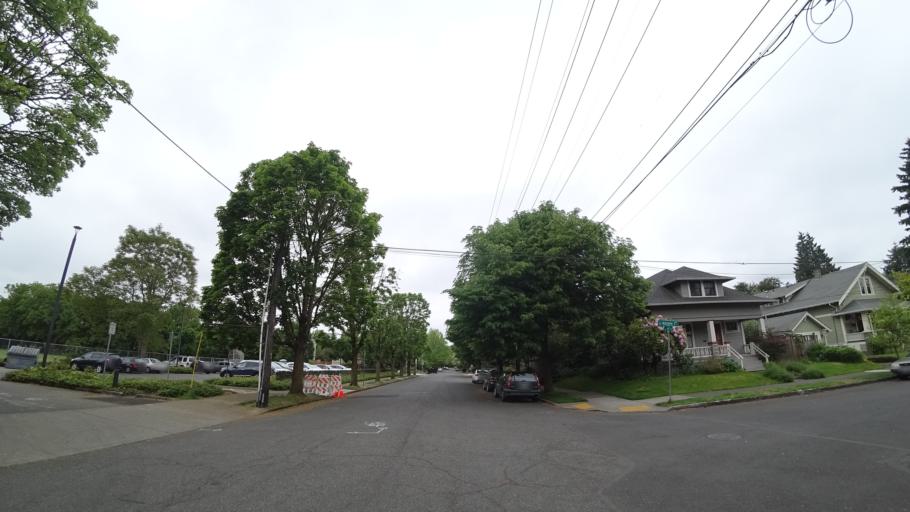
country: US
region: Oregon
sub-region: Clackamas County
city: Milwaukie
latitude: 45.4623
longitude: -122.6510
